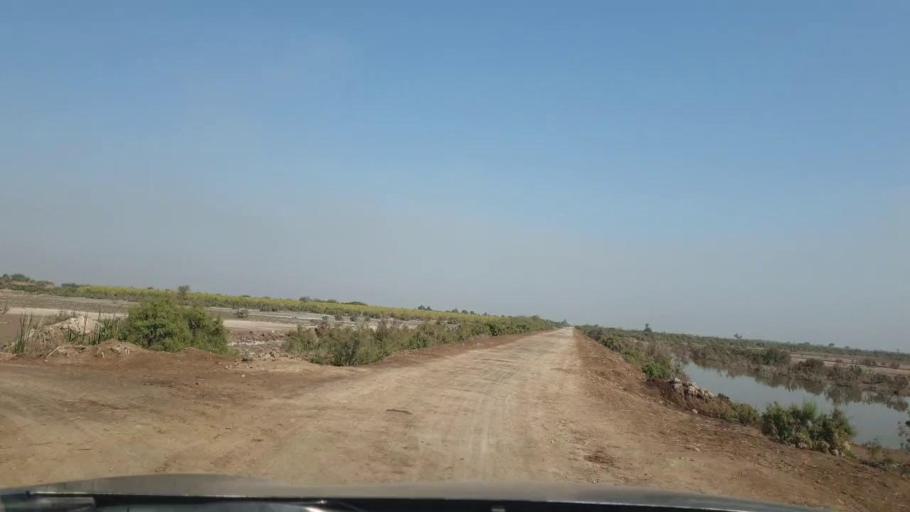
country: PK
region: Sindh
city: Berani
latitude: 25.6451
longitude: 68.8740
